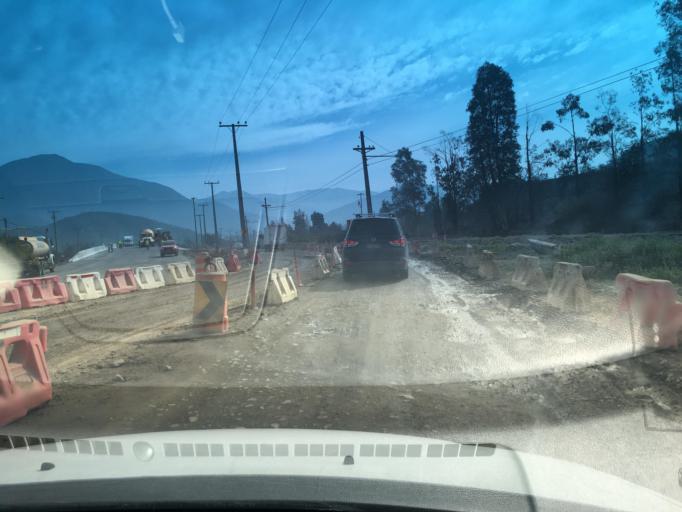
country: CL
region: Santiago Metropolitan
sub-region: Provincia de Chacabuco
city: Lampa
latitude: -33.1065
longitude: -70.9294
